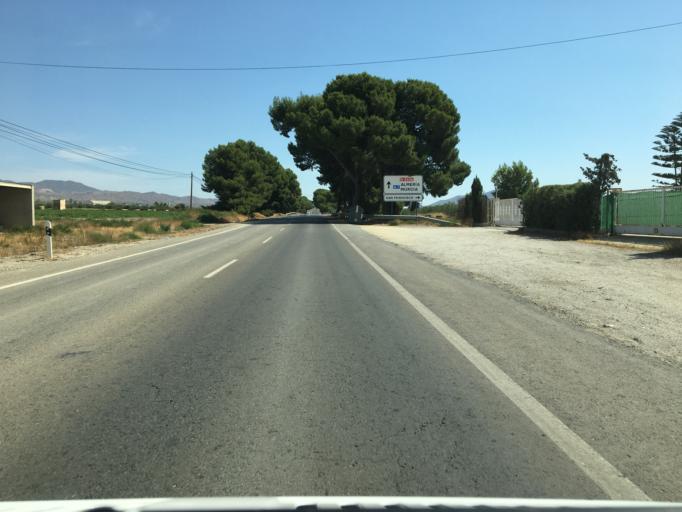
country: ES
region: Andalusia
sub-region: Provincia de Almeria
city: Huercal-Overa
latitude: 37.4205
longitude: -1.9212
